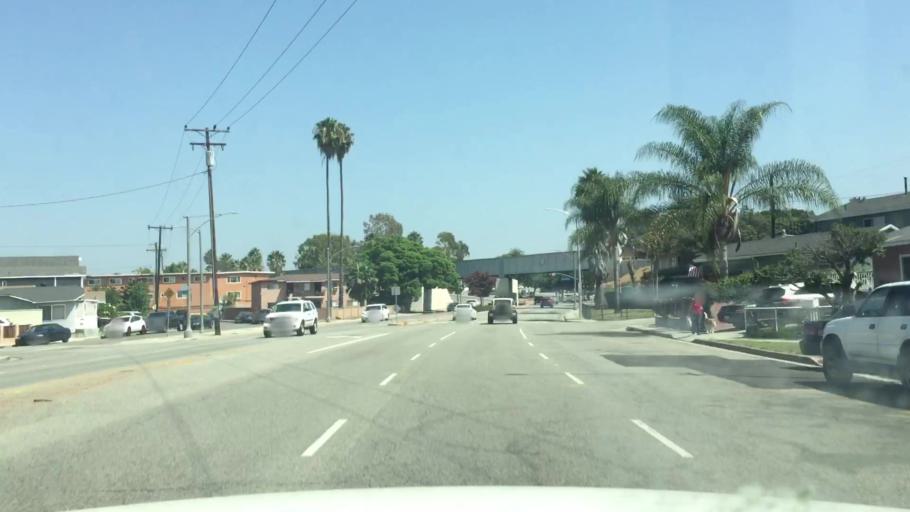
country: US
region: California
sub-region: Los Angeles County
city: Signal Hill
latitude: 33.8462
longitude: -118.1888
